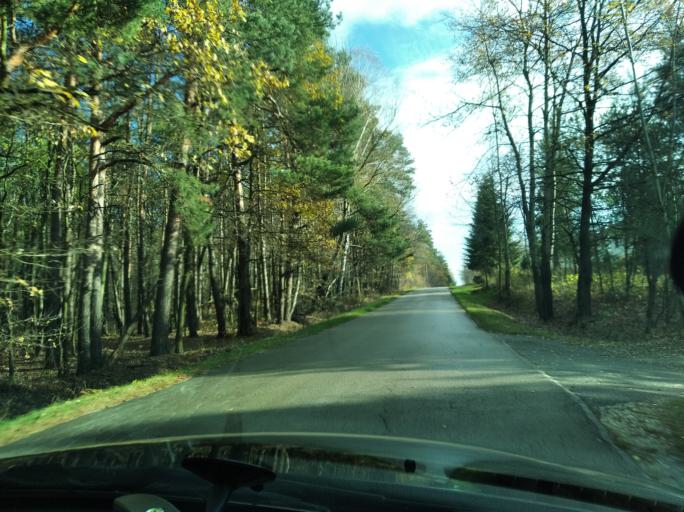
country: PL
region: Subcarpathian Voivodeship
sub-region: Powiat ropczycko-sedziszowski
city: Sedziszow Malopolski
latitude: 50.1206
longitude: 21.7204
